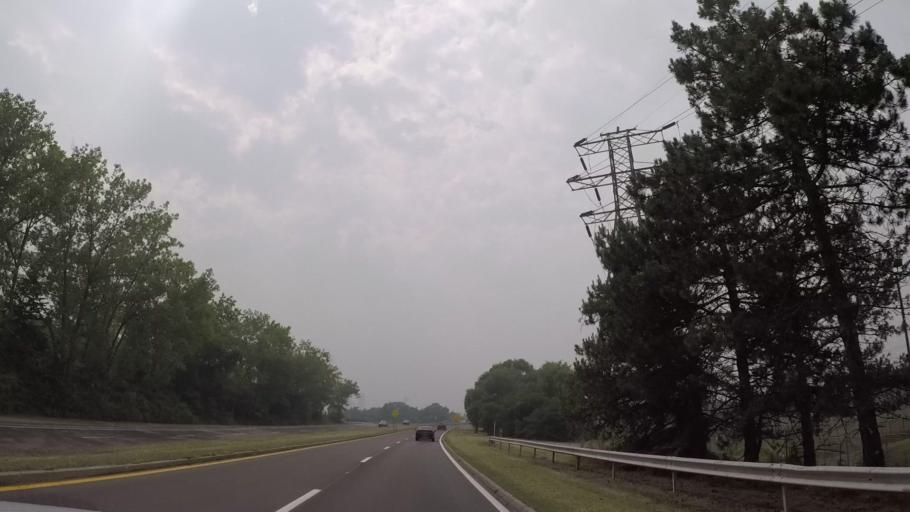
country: US
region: New York
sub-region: Niagara County
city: Niagara Falls
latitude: 43.0786
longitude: -79.0416
